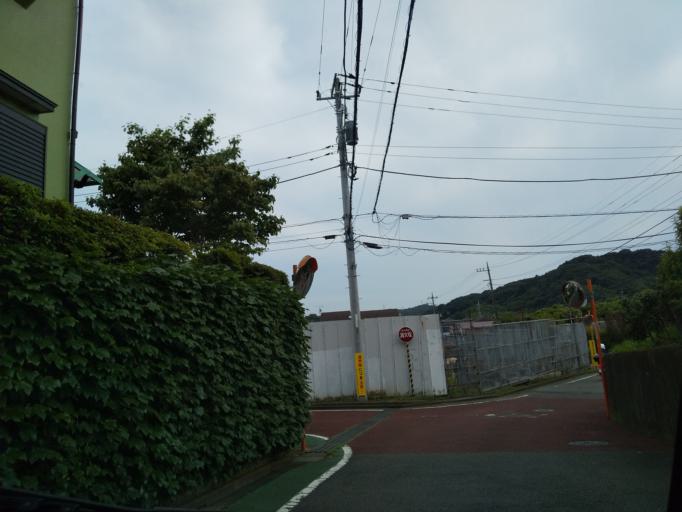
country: JP
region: Kanagawa
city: Atsugi
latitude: 35.4722
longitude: 139.3224
